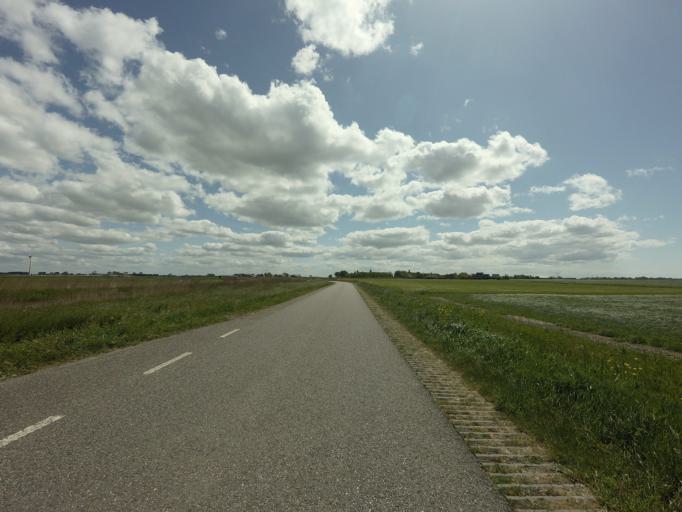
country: NL
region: Friesland
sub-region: Sudwest Fryslan
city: Makkum
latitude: 53.0899
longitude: 5.4171
